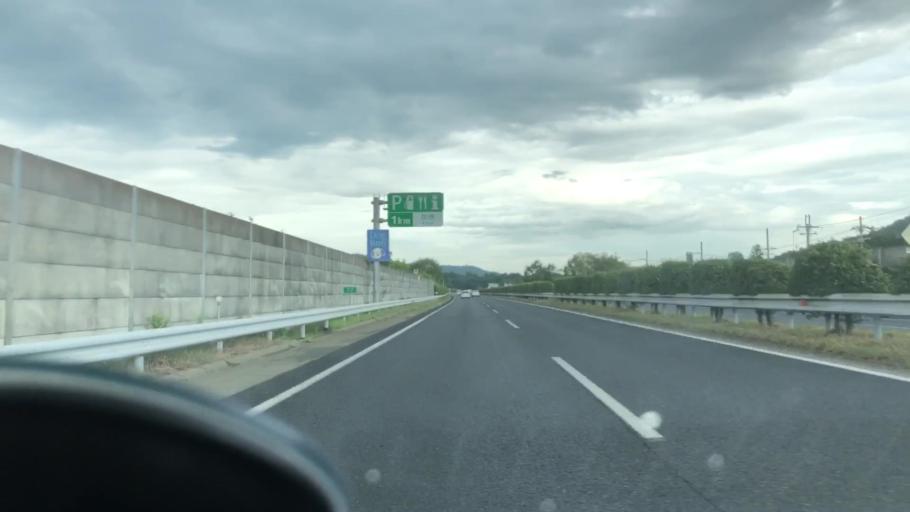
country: JP
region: Hyogo
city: Himeji
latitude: 34.9477
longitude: 134.7873
